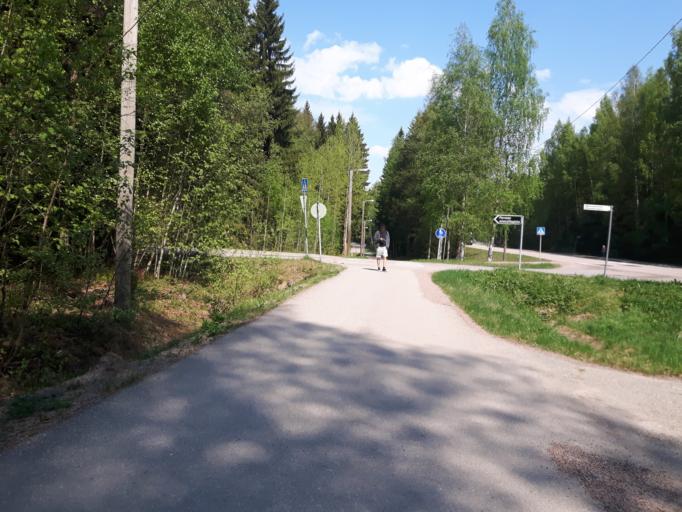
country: FI
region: Uusimaa
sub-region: Porvoo
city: Porvoo
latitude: 60.3874
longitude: 25.6300
